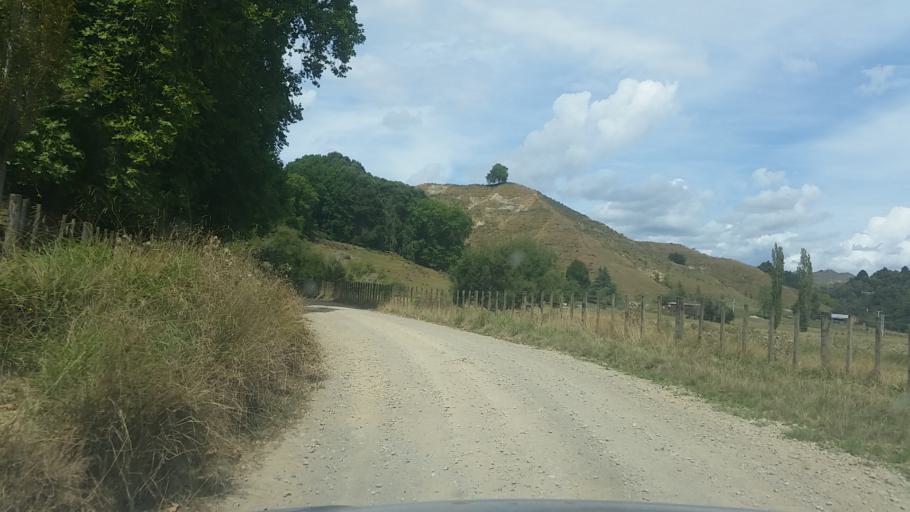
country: NZ
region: Taranaki
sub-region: New Plymouth District
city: Waitara
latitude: -39.0869
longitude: 174.8434
